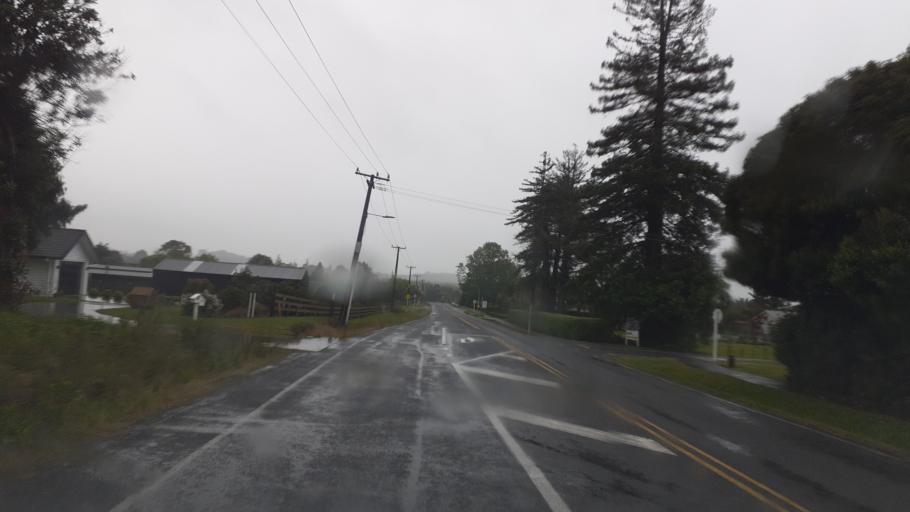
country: NZ
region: Northland
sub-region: Far North District
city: Kerikeri
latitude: -35.2094
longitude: 173.9634
